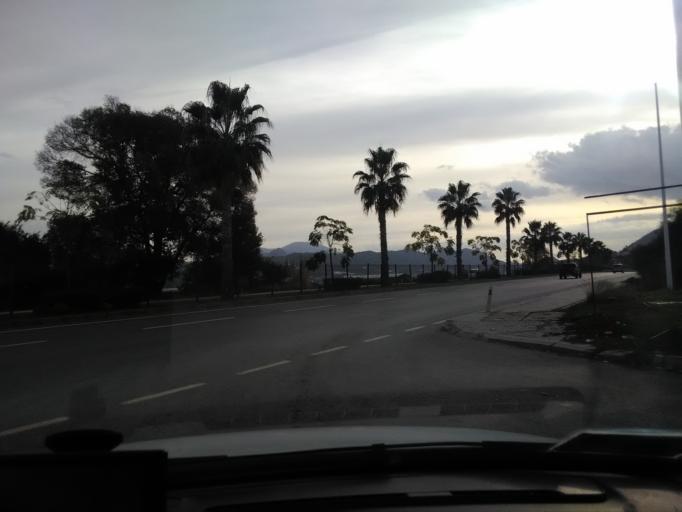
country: TR
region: Antalya
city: Gazipasa
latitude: 36.2621
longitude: 32.3206
